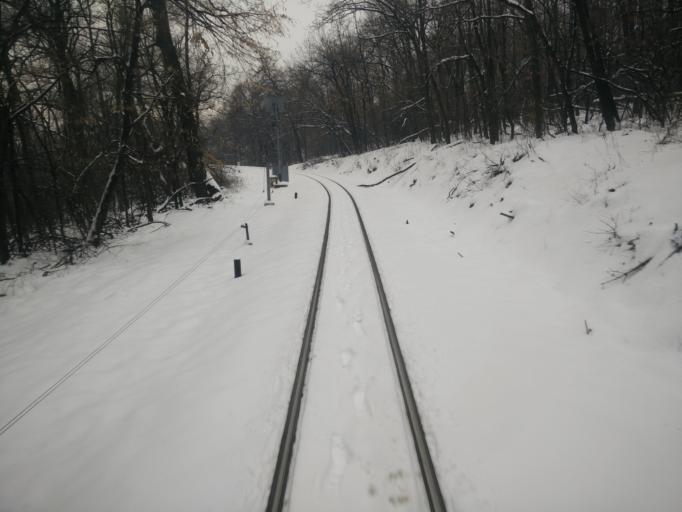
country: HU
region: Pest
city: Budakeszi
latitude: 47.5087
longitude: 18.9526
